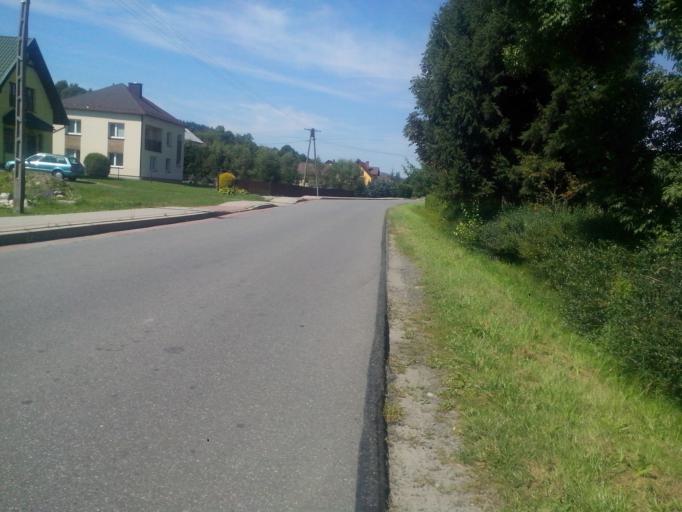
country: PL
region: Subcarpathian Voivodeship
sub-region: Powiat strzyzowski
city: Frysztak
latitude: 49.8644
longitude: 21.6239
